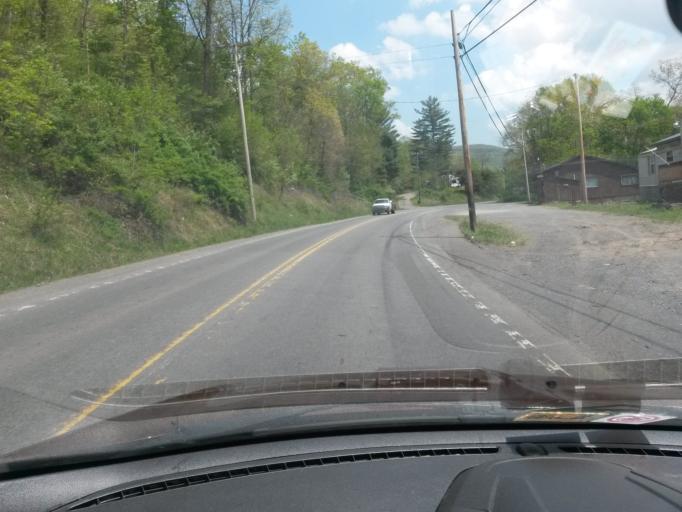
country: US
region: West Virginia
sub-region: Greenbrier County
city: Rainelle
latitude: 37.9870
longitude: -80.7274
